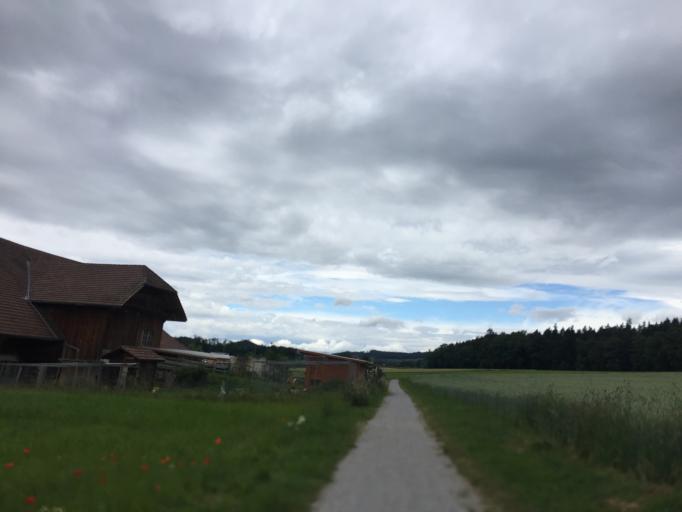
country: CH
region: Bern
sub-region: Bern-Mittelland District
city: Rubigen
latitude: 46.9021
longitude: 7.5467
